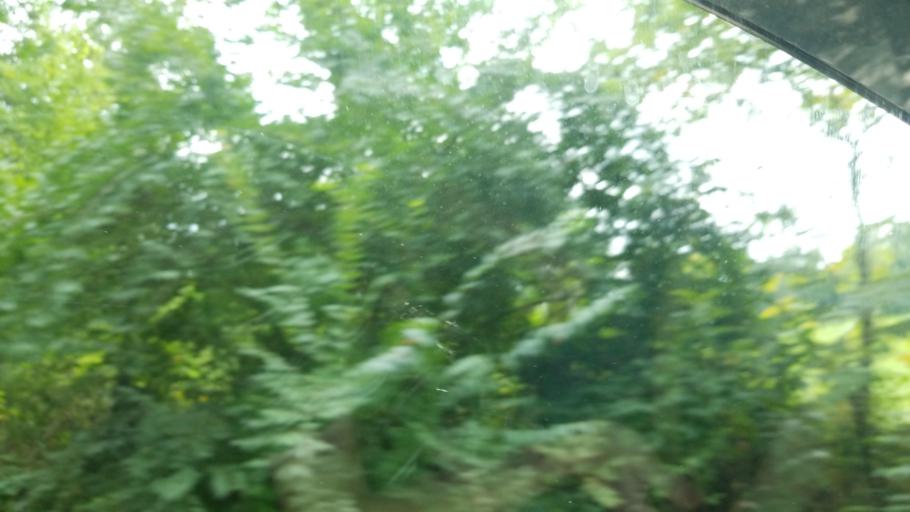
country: US
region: Illinois
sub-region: Saline County
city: Harrisburg
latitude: 37.8524
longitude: -88.6099
